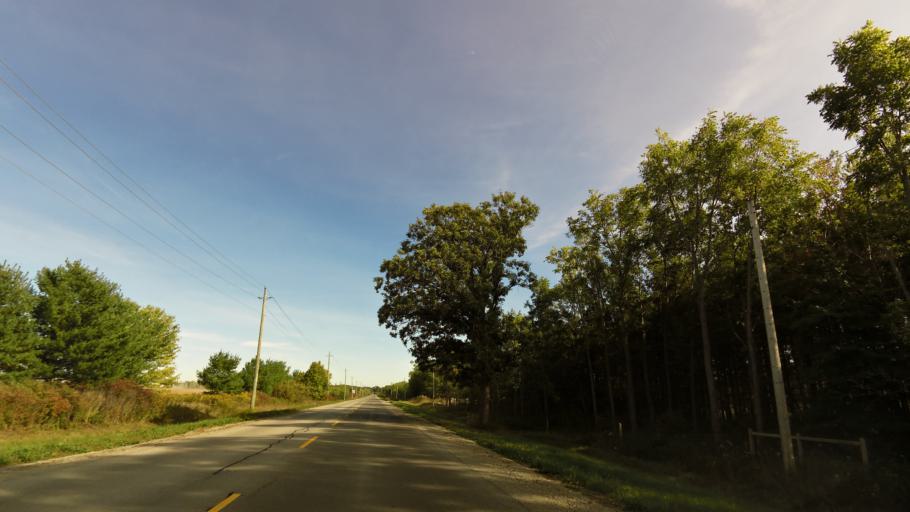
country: CA
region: Ontario
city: Ancaster
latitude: 43.0277
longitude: -80.0065
